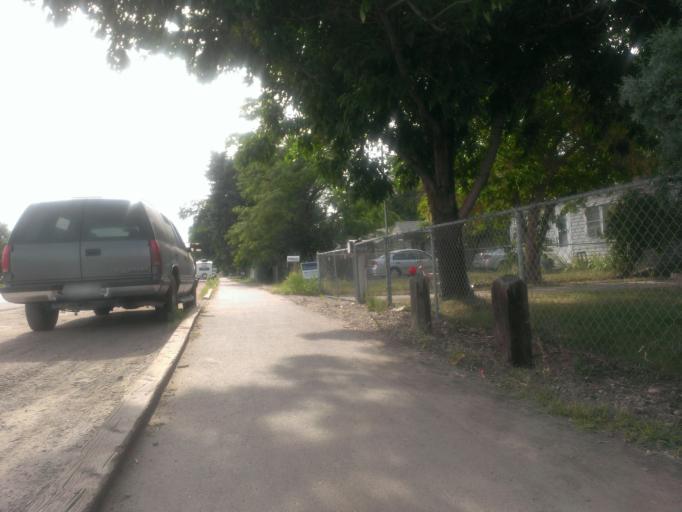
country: US
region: Colorado
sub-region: Larimer County
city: Fort Collins
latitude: 40.5889
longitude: -105.0649
